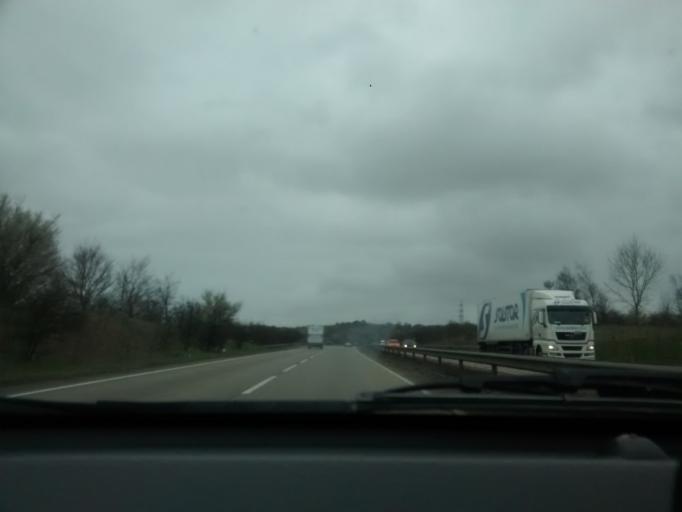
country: GB
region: England
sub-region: Suffolk
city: Bramford
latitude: 52.0650
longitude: 1.1088
